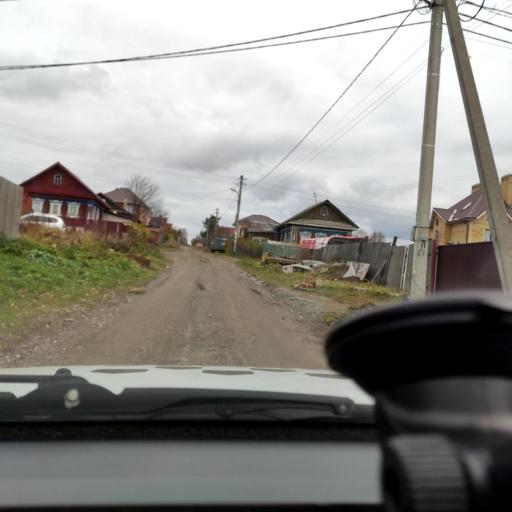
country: RU
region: Perm
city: Kondratovo
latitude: 58.0465
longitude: 56.1174
